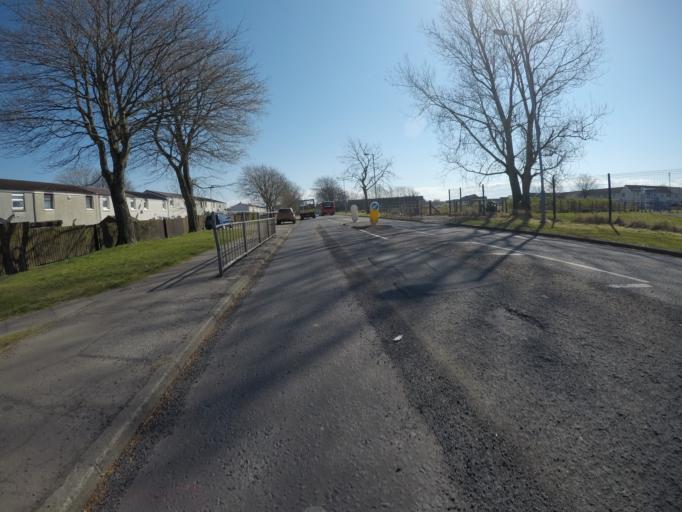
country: GB
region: Scotland
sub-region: North Ayrshire
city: Irvine
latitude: 55.6292
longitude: -4.6637
